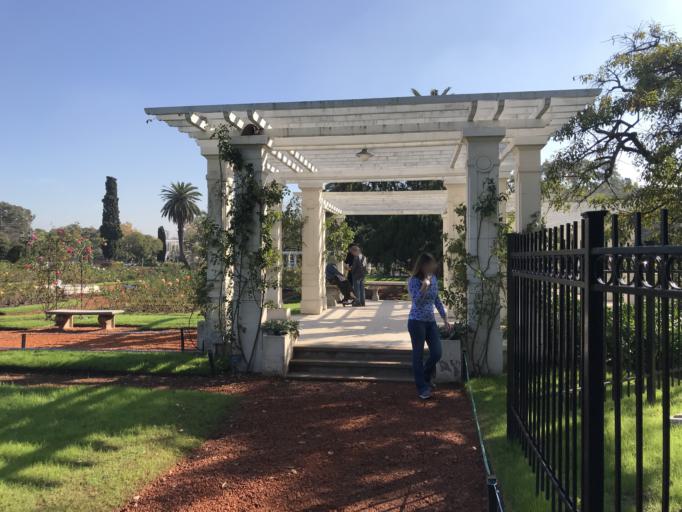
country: AR
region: Buenos Aires F.D.
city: Colegiales
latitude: -34.5706
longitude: -58.4166
